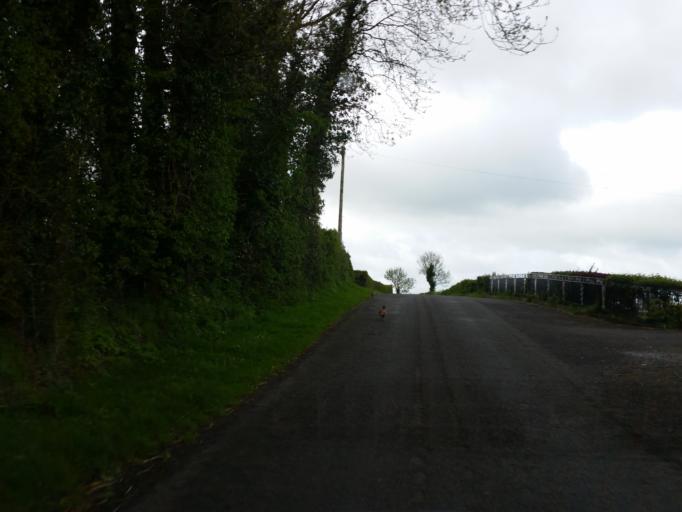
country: GB
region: Northern Ireland
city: Lisnaskea
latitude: 54.3256
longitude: -7.3915
